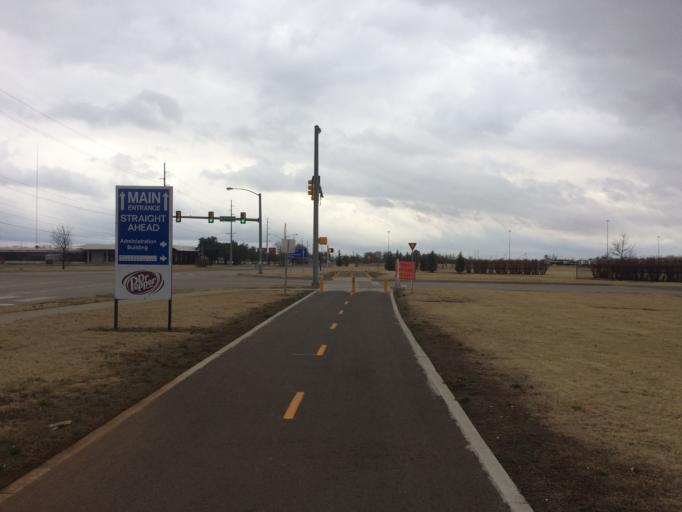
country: US
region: Oklahoma
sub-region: Oklahoma County
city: Oklahoma City
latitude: 35.4747
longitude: -97.5659
